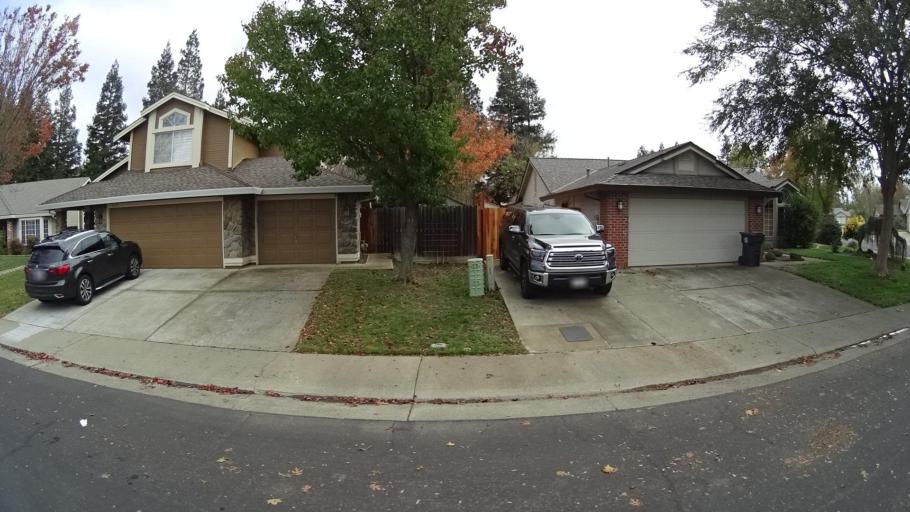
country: US
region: California
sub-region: Sacramento County
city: Elk Grove
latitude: 38.4222
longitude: -121.3599
